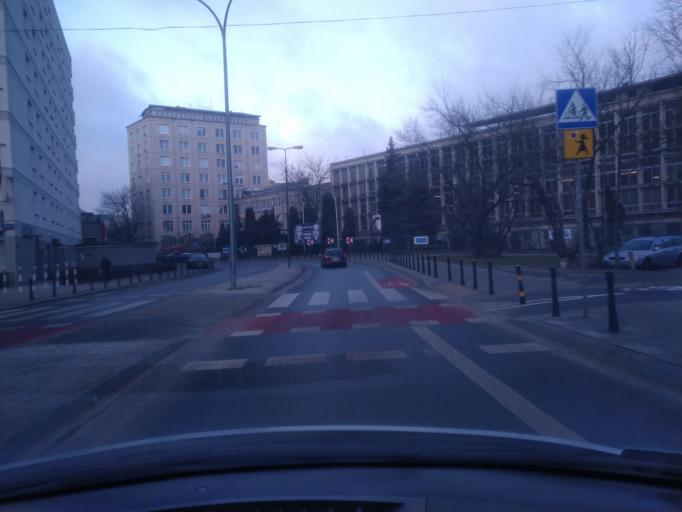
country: PL
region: Masovian Voivodeship
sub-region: Warszawa
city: Praga Poludnie
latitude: 52.2504
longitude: 21.0687
